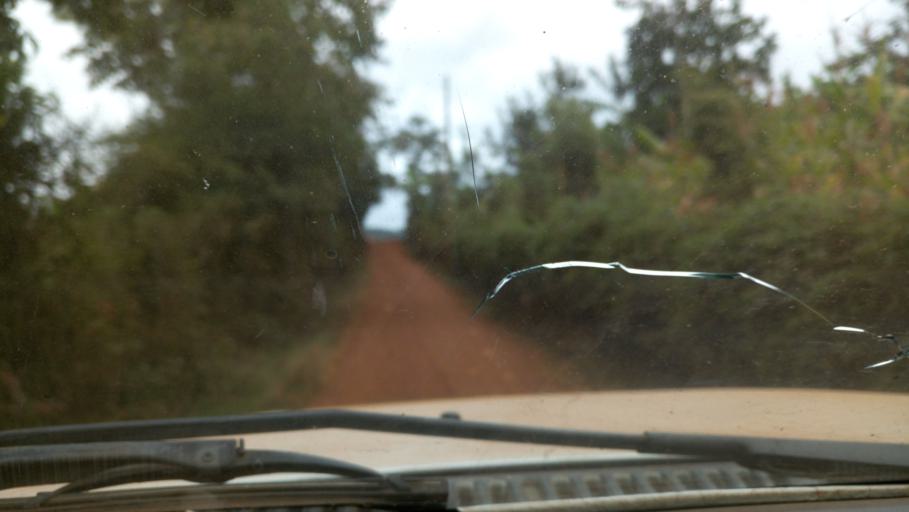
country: KE
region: Murang'a District
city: Maragua
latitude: -0.7733
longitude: 37.0804
